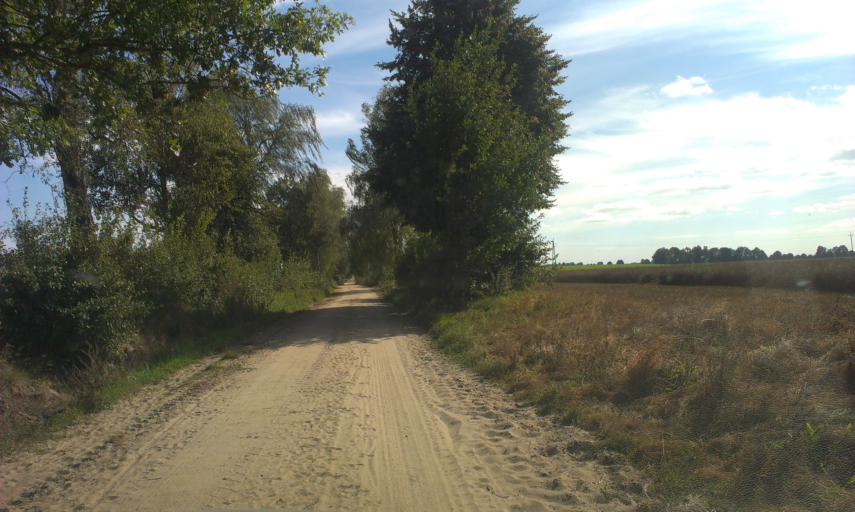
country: PL
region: Greater Poland Voivodeship
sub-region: Powiat pilski
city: Lobzenica
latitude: 53.2954
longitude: 17.1522
